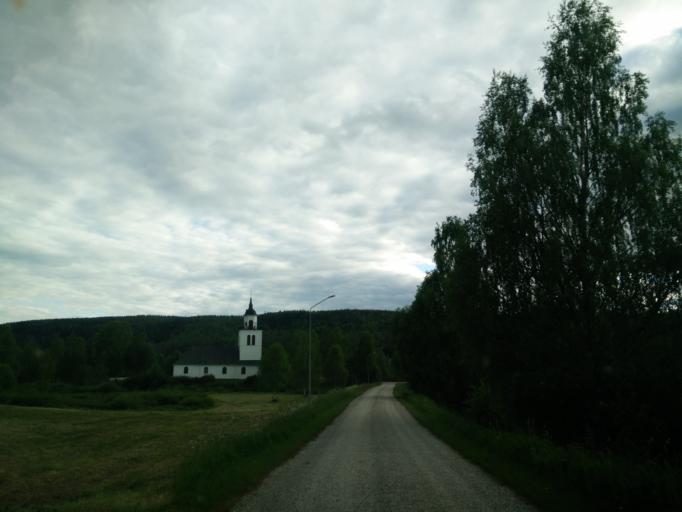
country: SE
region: Jaemtland
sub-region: Harjedalens Kommun
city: Sveg
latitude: 62.2783
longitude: 14.8063
